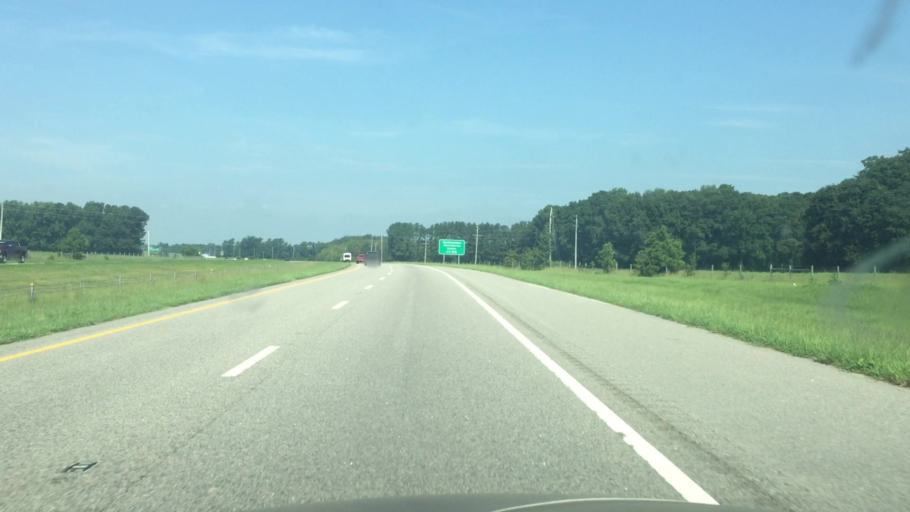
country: US
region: North Carolina
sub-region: Robeson County
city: Lumberton
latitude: 34.5915
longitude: -79.0714
